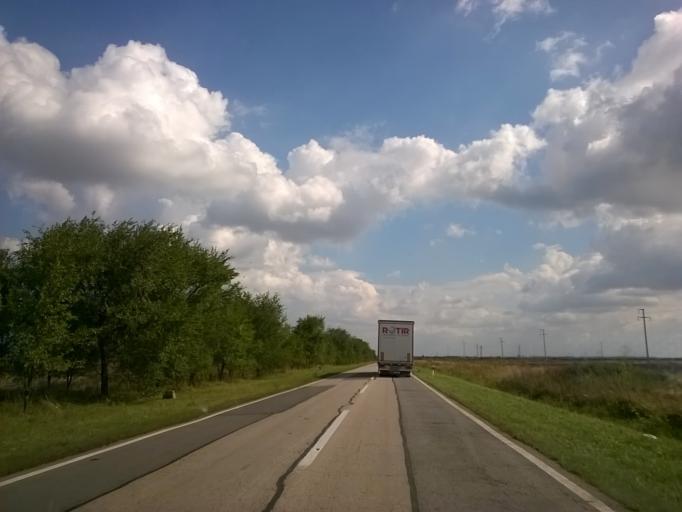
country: RS
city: Pavlis
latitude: 45.1619
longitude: 21.2376
